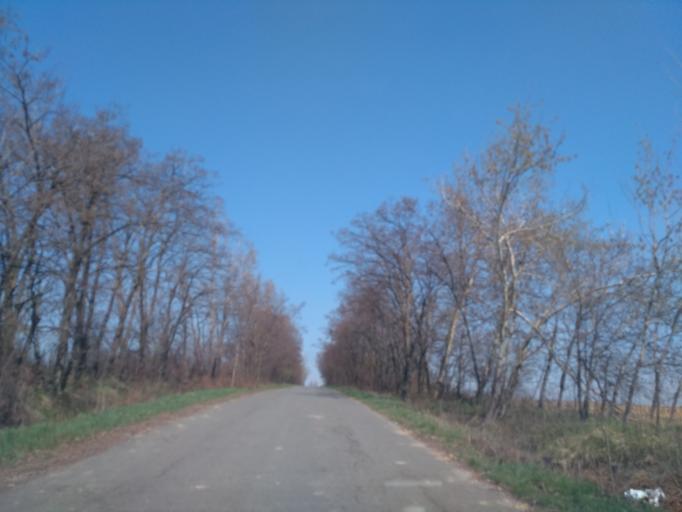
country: SK
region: Presovsky
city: Vranov nad Topl'ou
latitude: 48.8076
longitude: 21.6391
